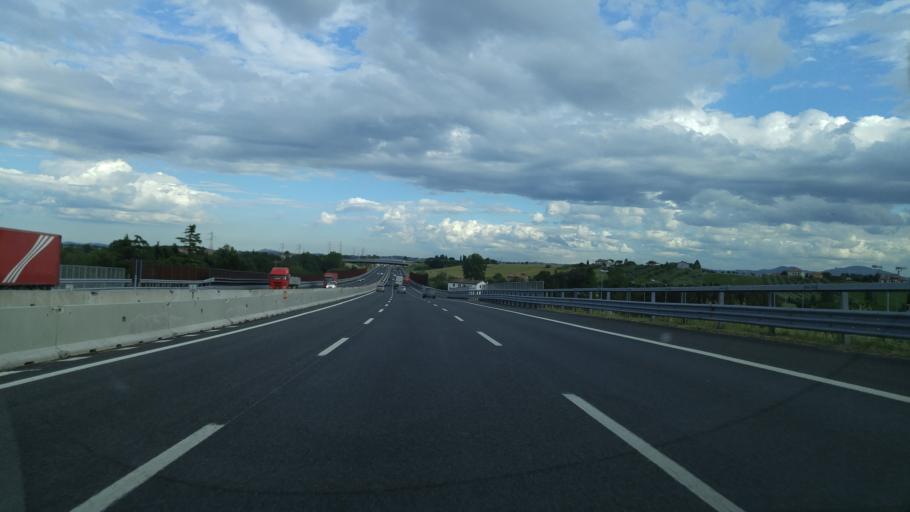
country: IT
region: Emilia-Romagna
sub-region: Provincia di Rimini
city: Rivazzurra
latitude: 44.0159
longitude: 12.5880
